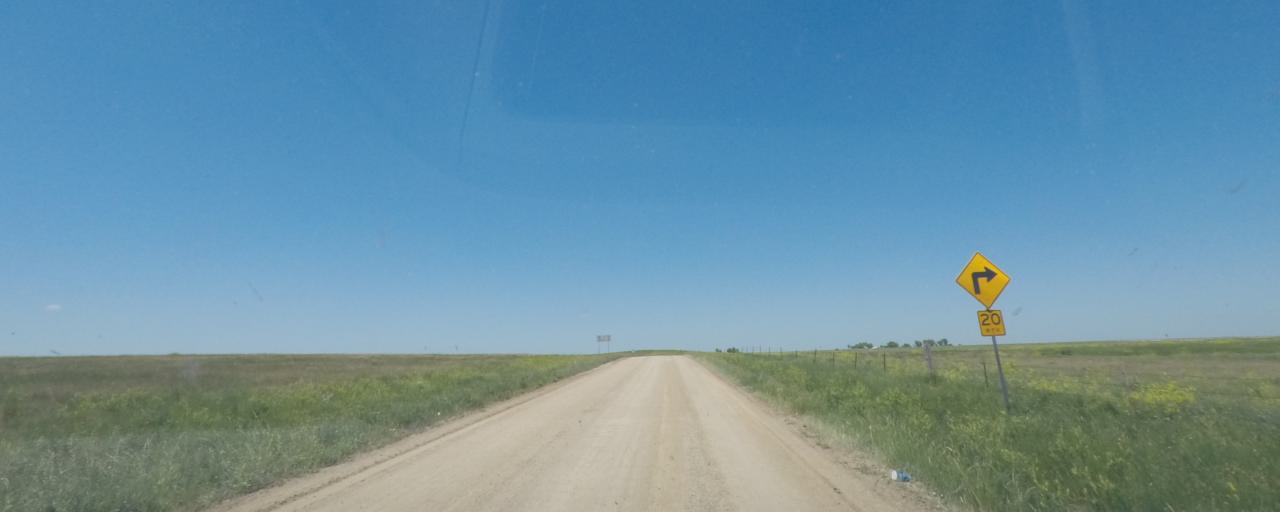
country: US
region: South Dakota
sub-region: Haakon County
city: Philip
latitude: 43.9348
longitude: -102.1587
